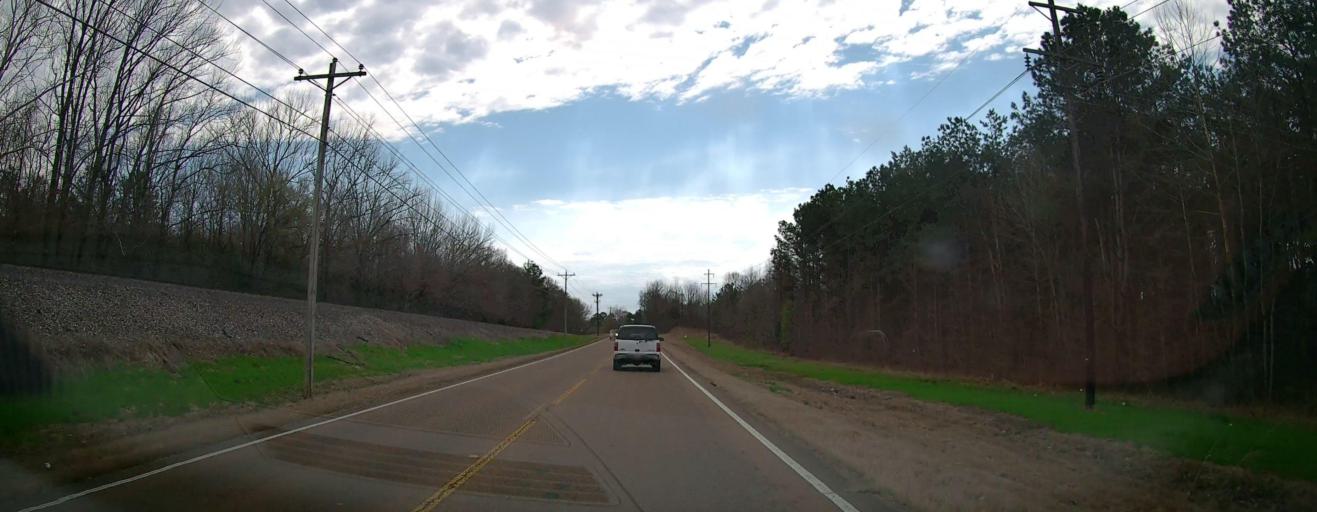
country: US
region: Mississippi
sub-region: Marshall County
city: Byhalia
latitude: 34.8930
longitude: -89.7351
